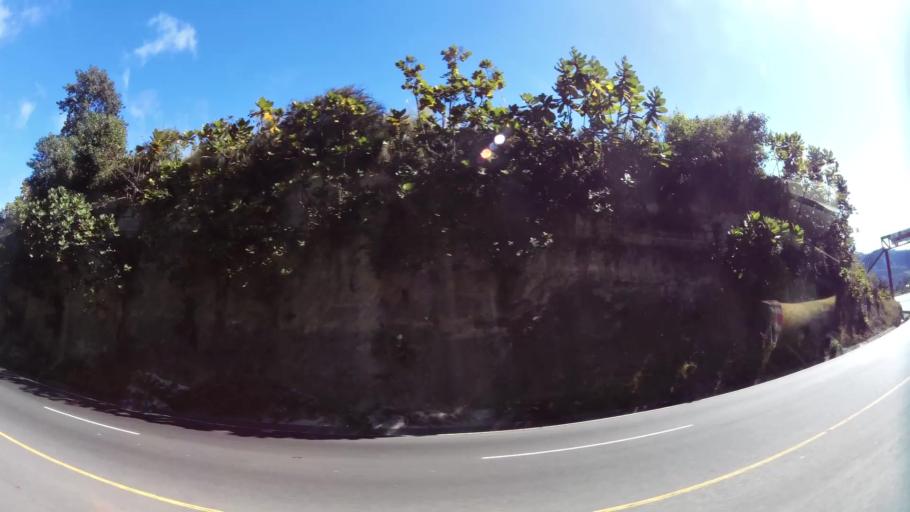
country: GT
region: Solola
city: Nahuala
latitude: 14.8196
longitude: -91.3360
